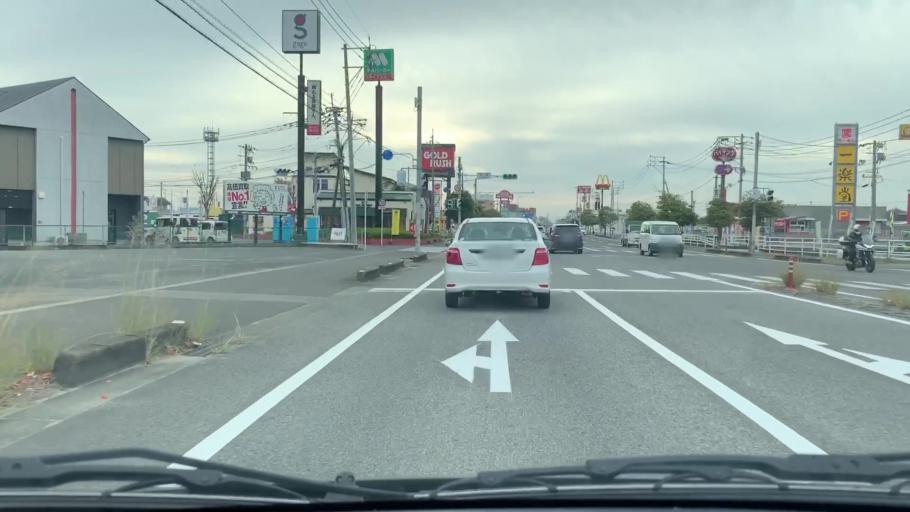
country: JP
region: Saga Prefecture
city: Saga-shi
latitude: 33.2946
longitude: 130.2839
